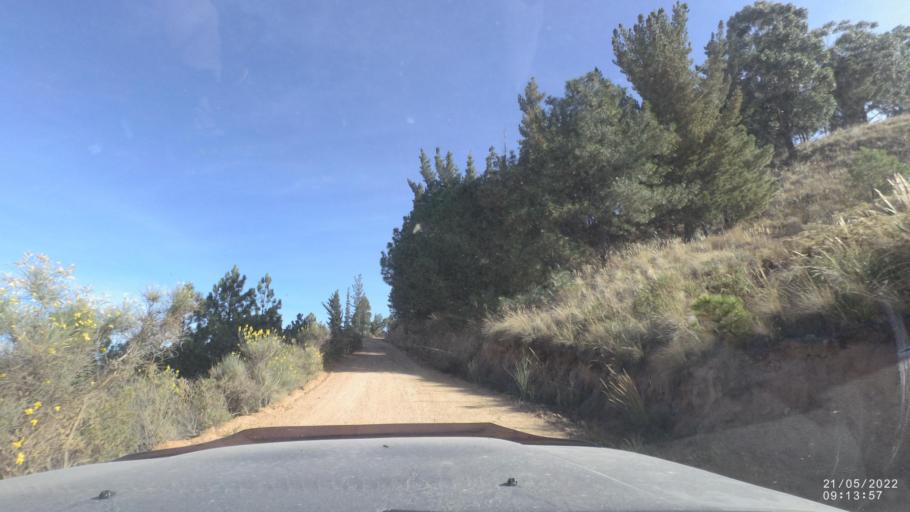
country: BO
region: Cochabamba
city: Cochabamba
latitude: -17.3666
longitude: -66.0282
